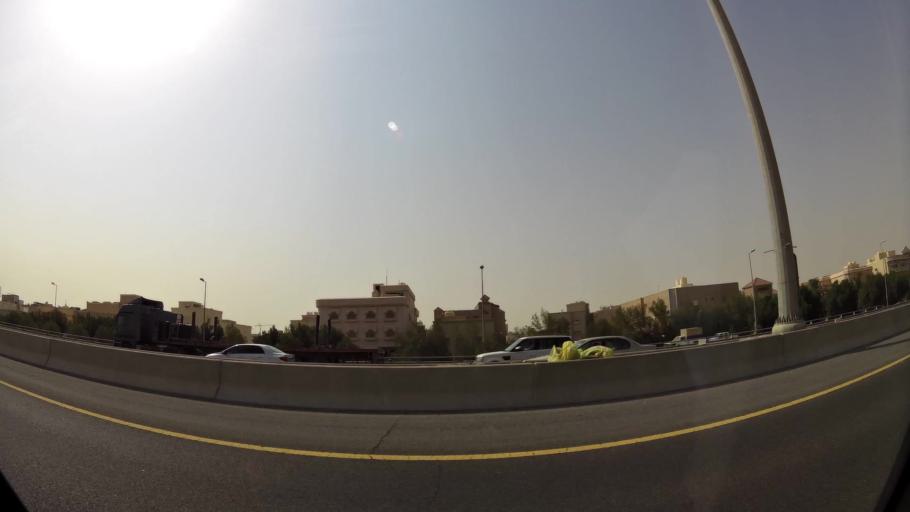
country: KW
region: Muhafazat al Jahra'
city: Al Jahra'
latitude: 29.3544
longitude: 47.6835
